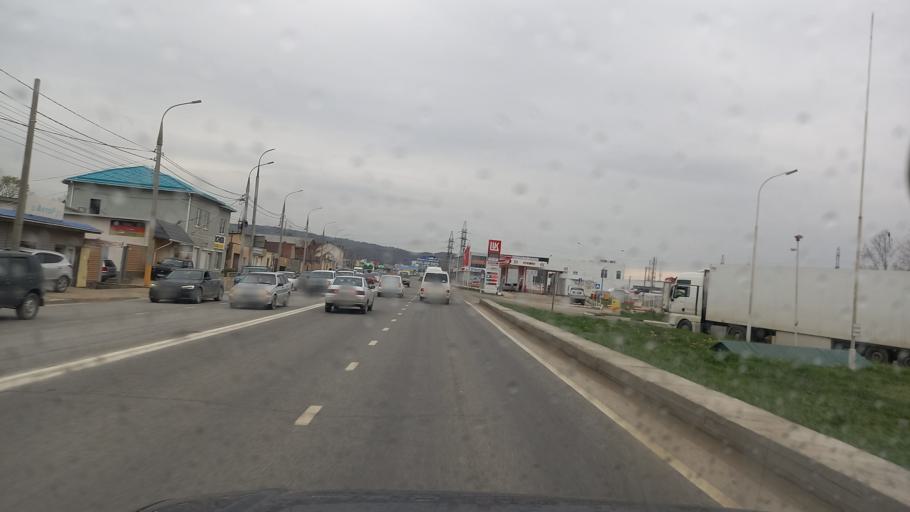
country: RU
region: Krasnodarskiy
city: Gayduk
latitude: 44.7663
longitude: 37.7119
